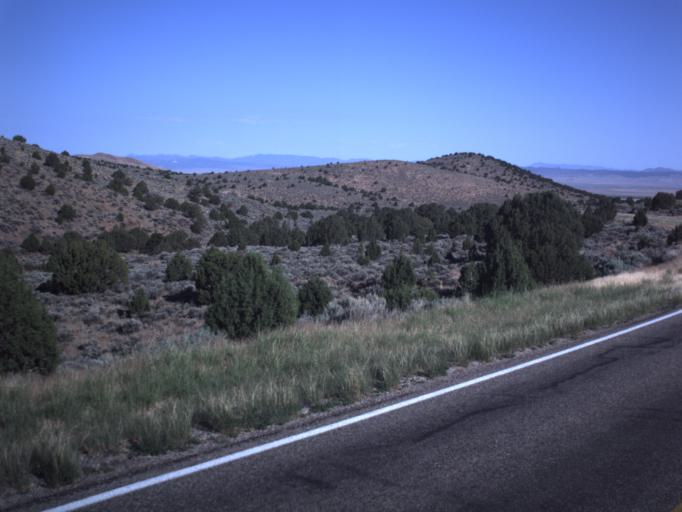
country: US
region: Utah
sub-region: Beaver County
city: Milford
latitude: 38.1223
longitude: -112.9513
